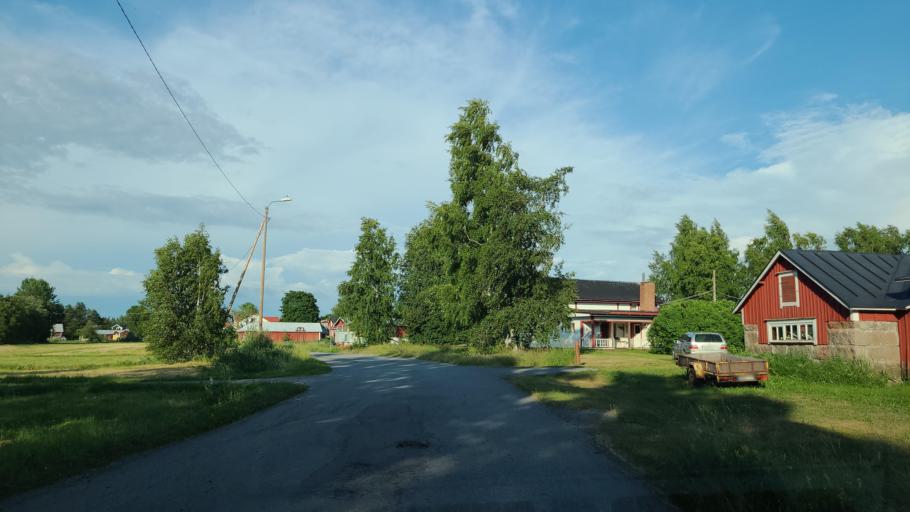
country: FI
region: Ostrobothnia
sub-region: Vaasa
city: Replot
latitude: 63.3447
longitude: 21.3295
